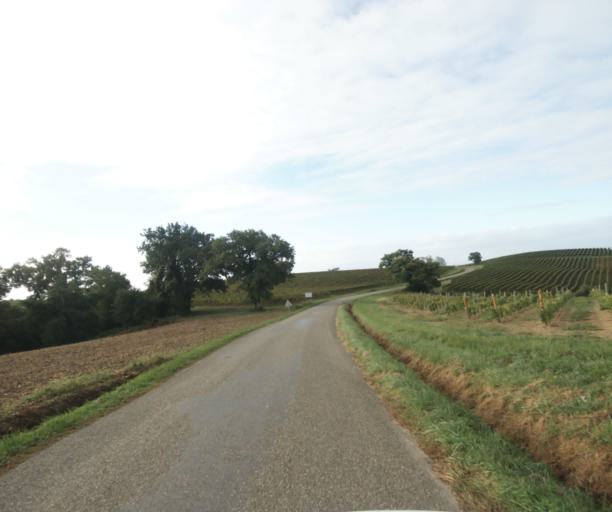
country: FR
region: Midi-Pyrenees
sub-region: Departement du Gers
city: Nogaro
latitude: 43.8307
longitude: -0.0324
